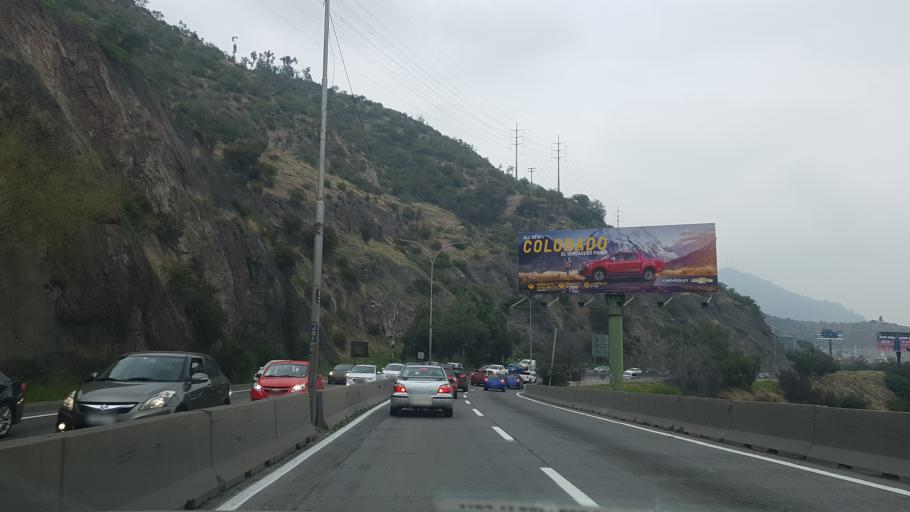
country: CL
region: Santiago Metropolitan
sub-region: Provincia de Santiago
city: Villa Presidente Frei, Nunoa, Santiago, Chile
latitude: -33.3919
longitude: -70.6071
